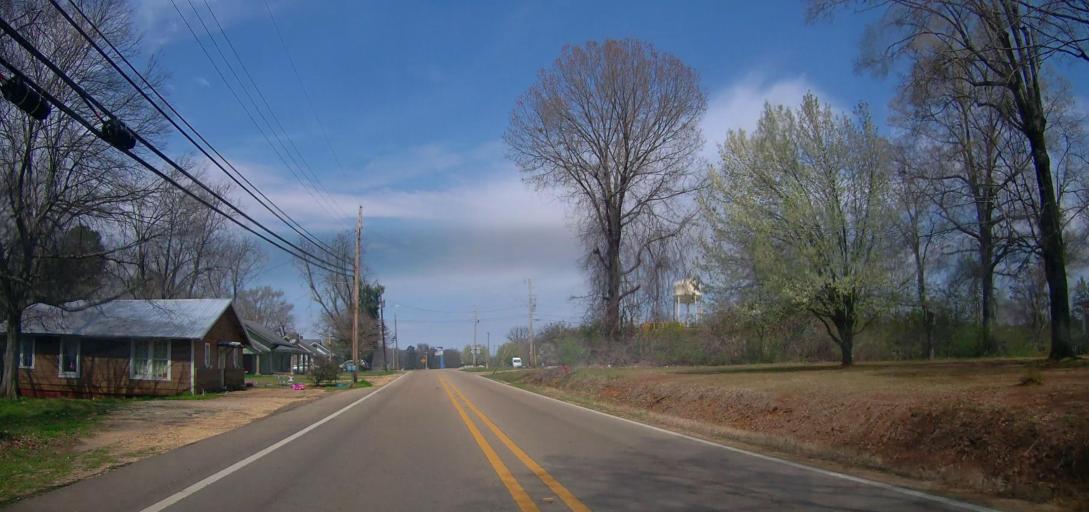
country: US
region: Mississippi
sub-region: Union County
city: New Albany
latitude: 34.4798
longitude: -88.9988
